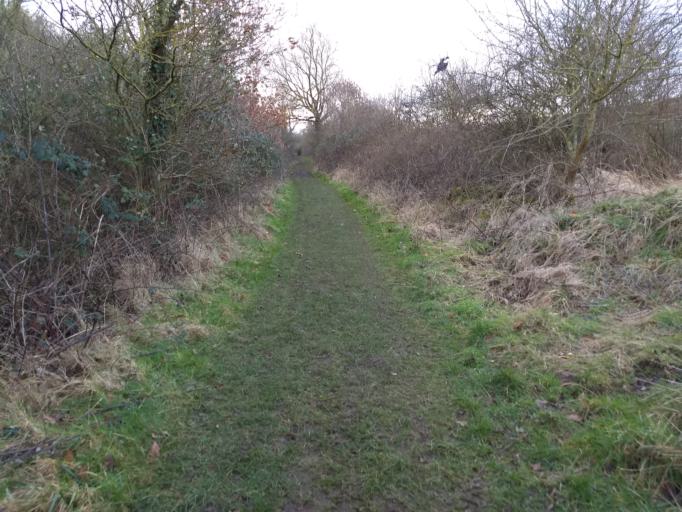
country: GB
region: England
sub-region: Buckinghamshire
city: Bletchley
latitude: 51.9862
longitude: -0.7399
